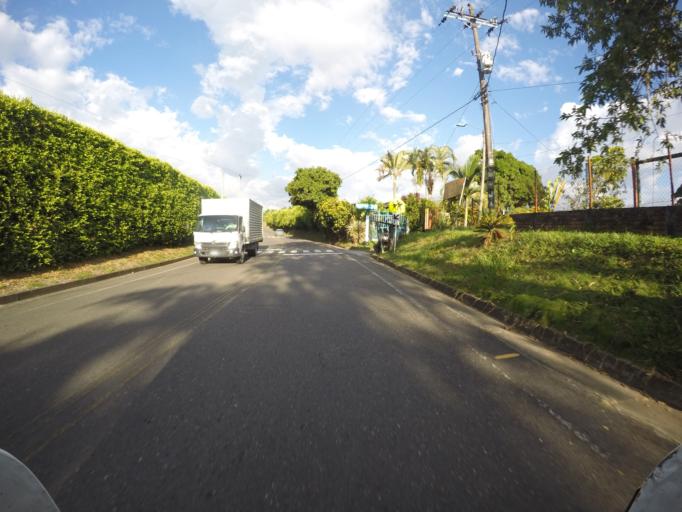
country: CO
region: Valle del Cauca
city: Alcala
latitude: 4.6879
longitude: -75.8186
